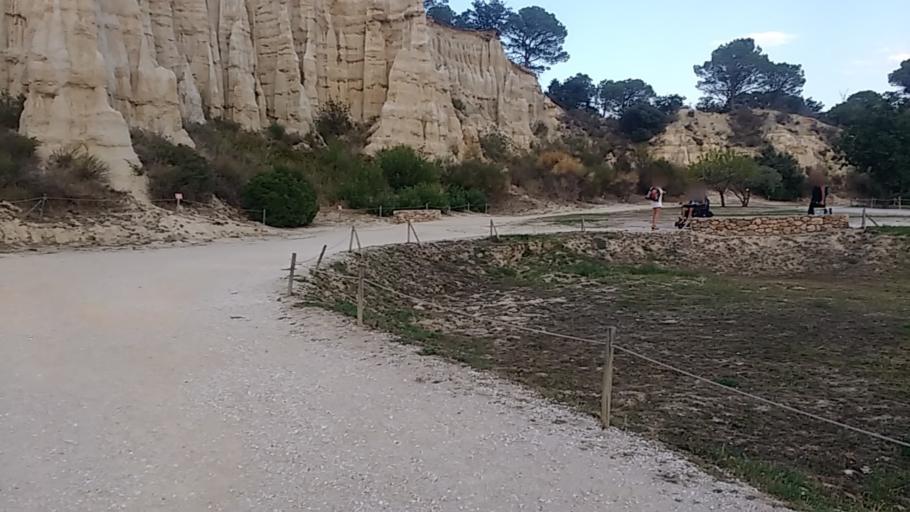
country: FR
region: Languedoc-Roussillon
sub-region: Departement des Pyrenees-Orientales
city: Ille-sur-Tet
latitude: 42.6863
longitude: 2.6213
